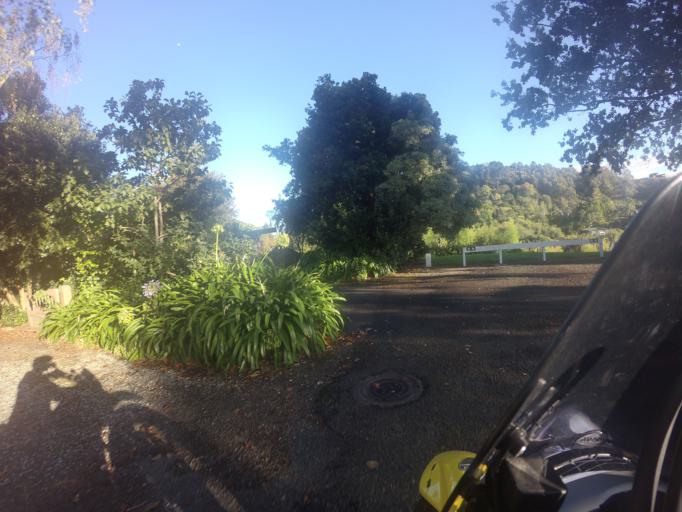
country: NZ
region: Gisborne
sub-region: Gisborne District
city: Gisborne
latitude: -38.6654
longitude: 178.0465
